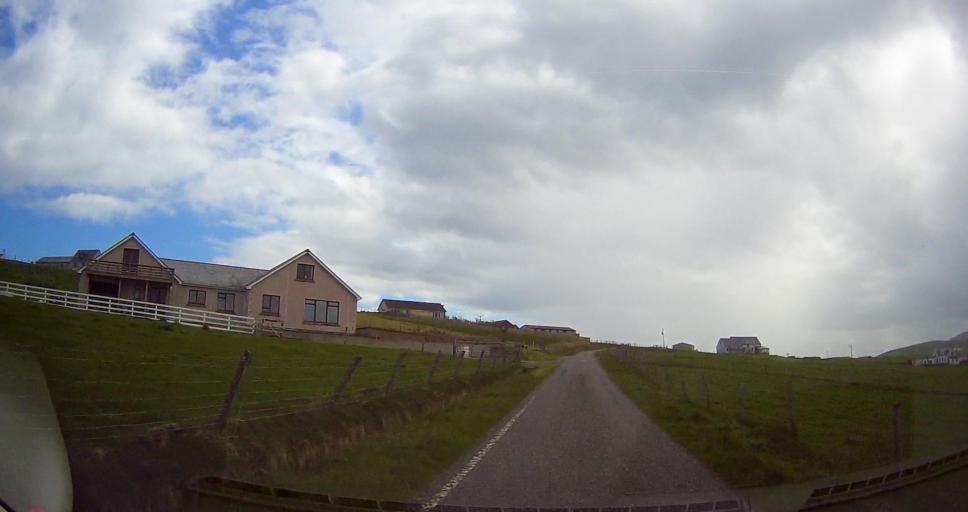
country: GB
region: Scotland
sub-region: Shetland Islands
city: Sandwick
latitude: 59.9183
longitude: -1.3203
